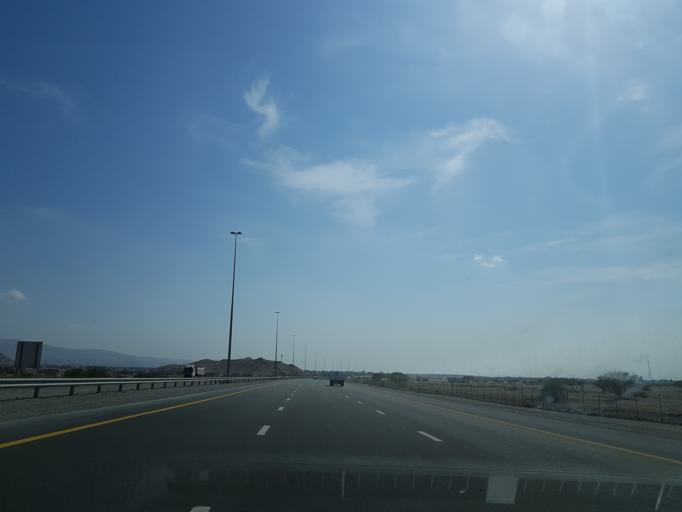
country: AE
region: Ra's al Khaymah
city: Ras al-Khaimah
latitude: 25.7385
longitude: 56.0154
